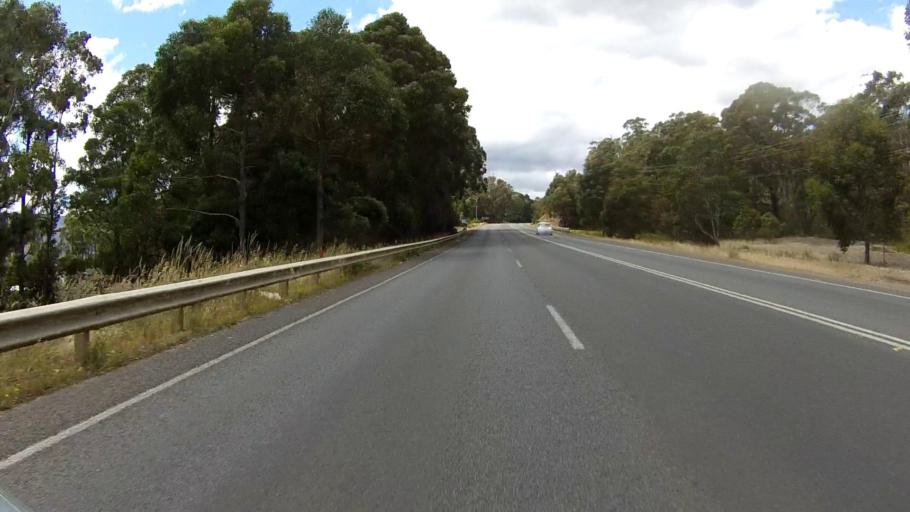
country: AU
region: Tasmania
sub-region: Huon Valley
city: Huonville
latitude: -42.9785
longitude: 147.1018
